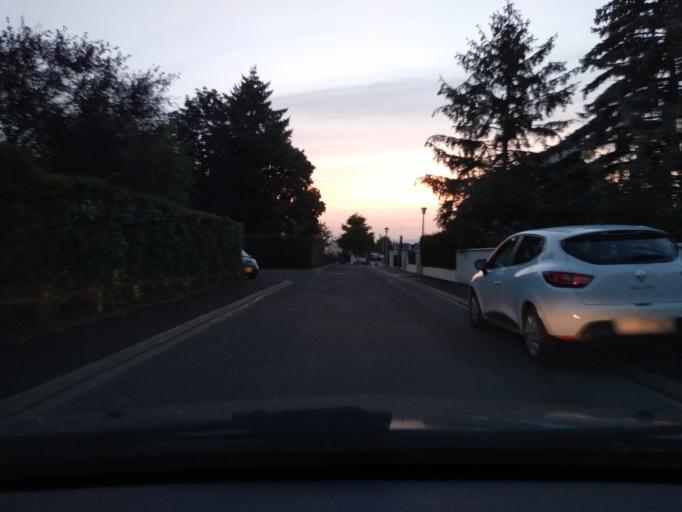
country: FR
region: Centre
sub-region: Departement d'Indre-et-Loire
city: Chanceaux-sur-Choisille
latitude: 47.4549
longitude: 0.7053
